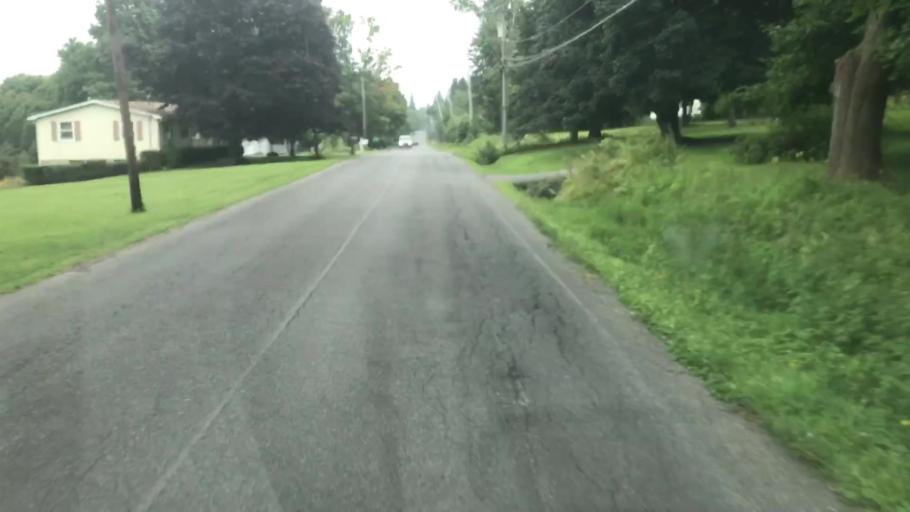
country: US
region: New York
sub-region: Onondaga County
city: Skaneateles
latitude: 42.9487
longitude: -76.4458
